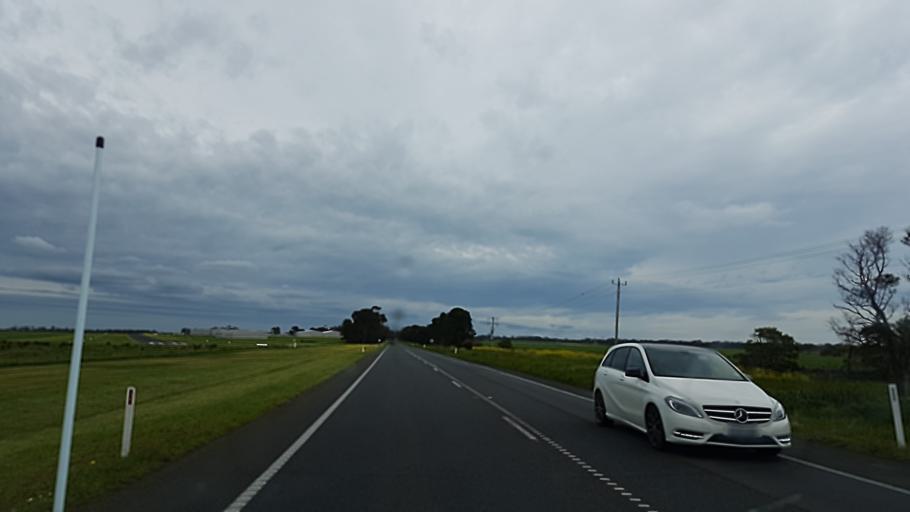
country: AU
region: Victoria
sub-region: Greater Geelong
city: Bell Post Hill
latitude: -37.9245
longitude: 144.1128
